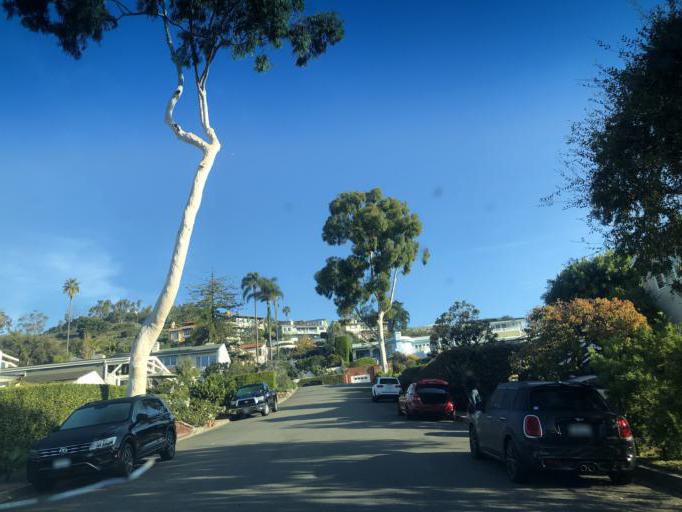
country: US
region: California
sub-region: Orange County
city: Laguna Beach
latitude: 33.5474
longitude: -117.7865
